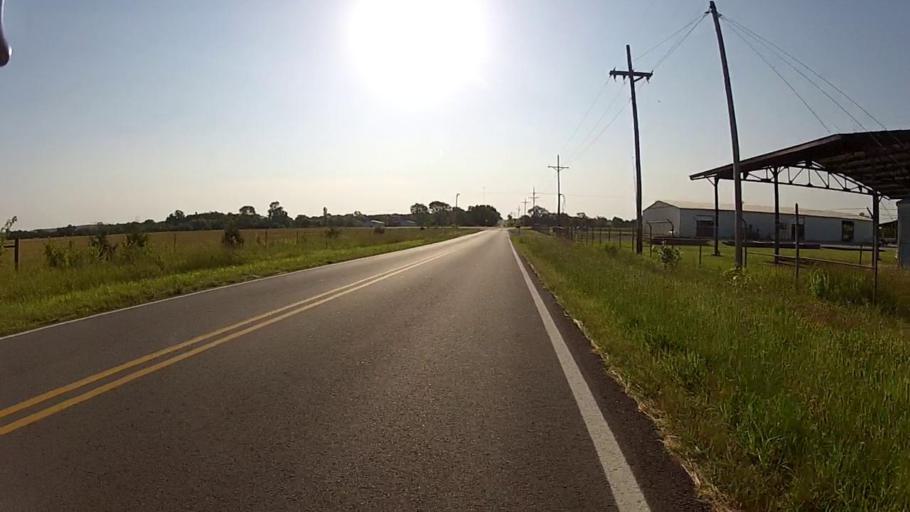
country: US
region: Kansas
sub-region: Montgomery County
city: Caney
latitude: 37.0963
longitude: -95.9302
